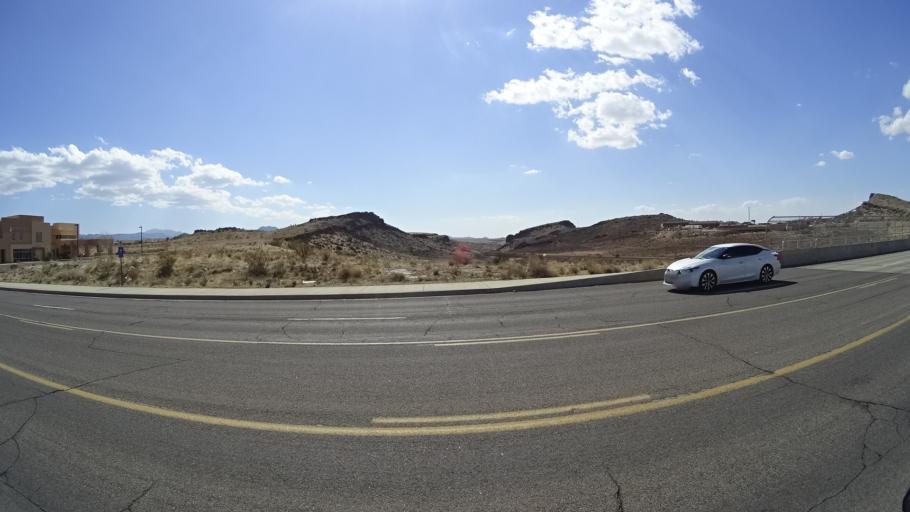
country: US
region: Arizona
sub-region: Mohave County
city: Kingman
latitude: 35.1936
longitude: -114.0281
